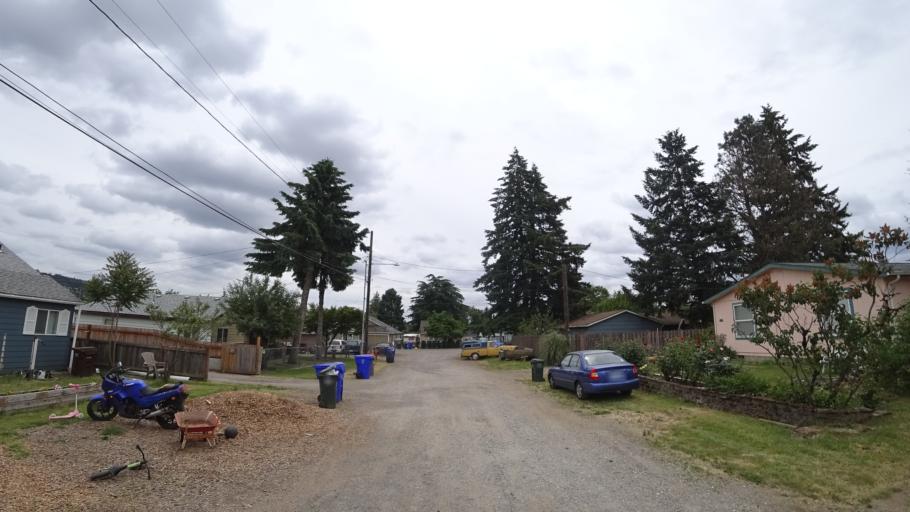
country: US
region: Oregon
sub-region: Multnomah County
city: Lents
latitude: 45.4638
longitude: -122.5849
